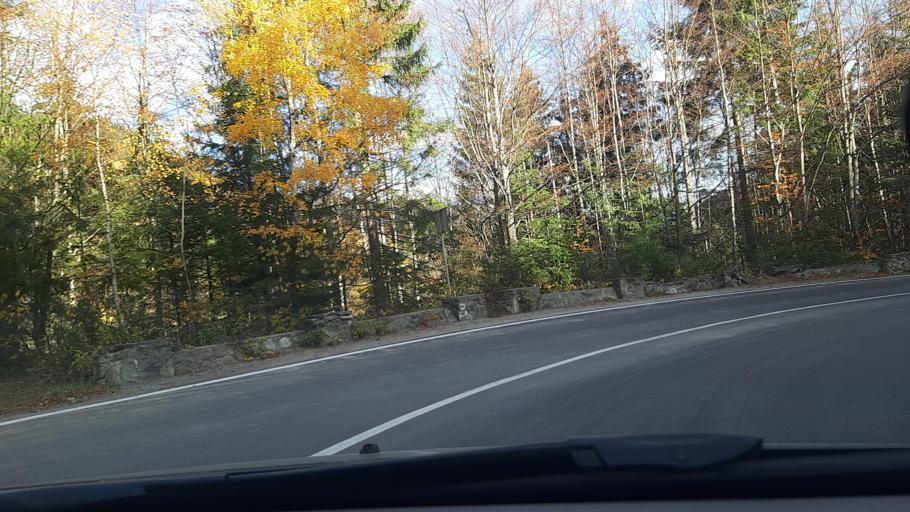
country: RO
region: Valcea
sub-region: Comuna Voineasa
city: Voineasa
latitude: 45.4358
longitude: 23.8604
